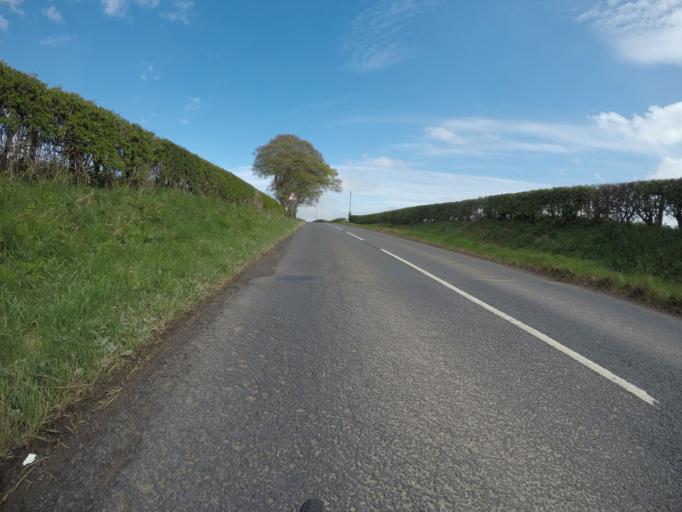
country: GB
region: Scotland
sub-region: East Ayrshire
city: Kilmaurs
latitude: 55.6528
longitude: -4.5636
